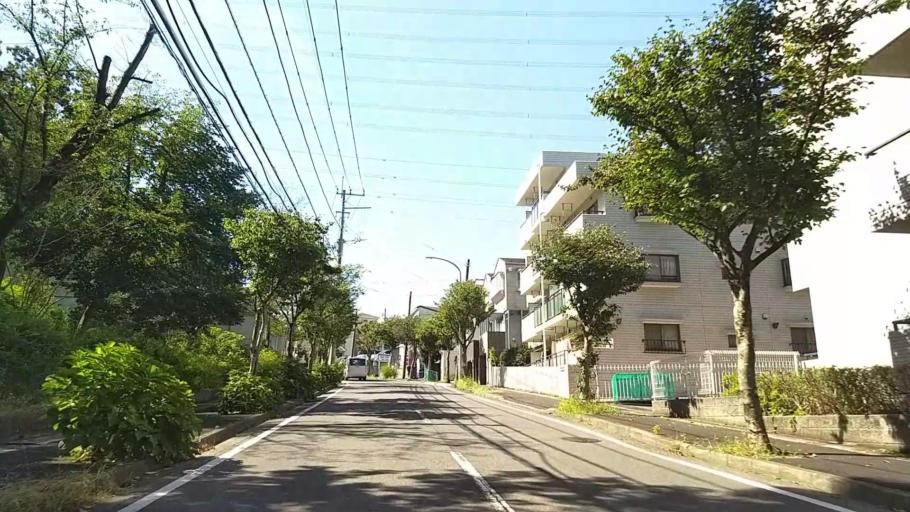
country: JP
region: Tokyo
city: Chofugaoka
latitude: 35.5711
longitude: 139.5382
